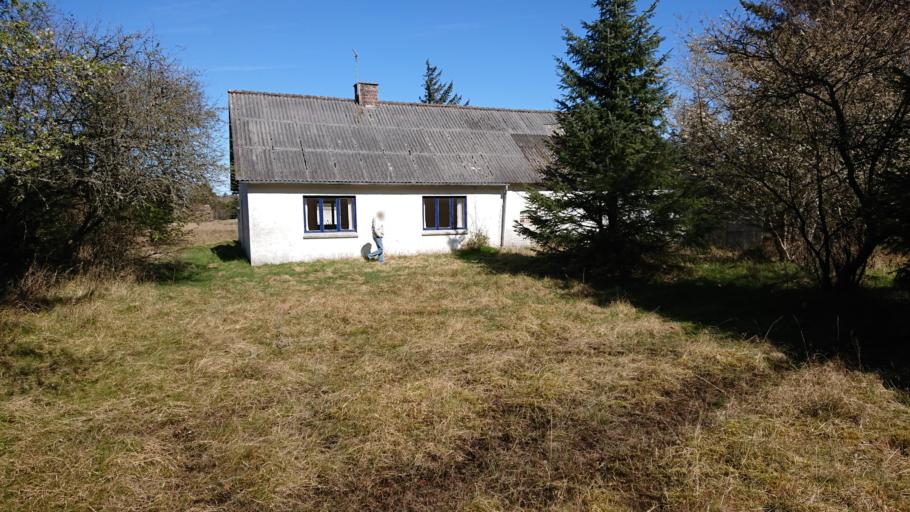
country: DK
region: North Denmark
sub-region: Frederikshavn Kommune
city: Skagen
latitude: 57.6514
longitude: 10.4232
